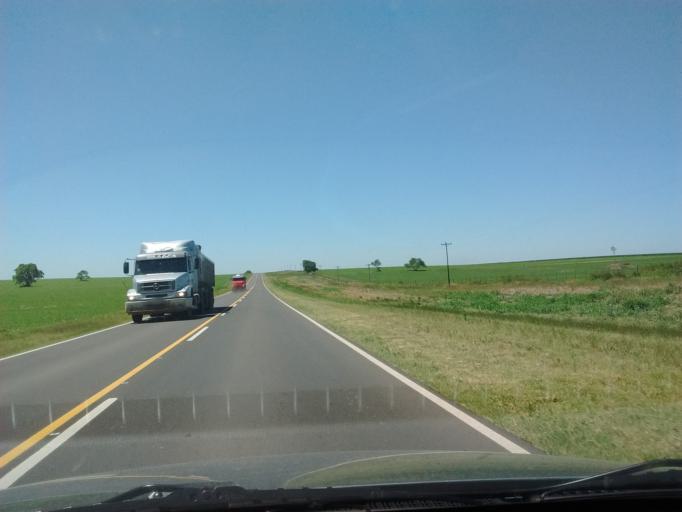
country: AR
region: Entre Rios
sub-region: Departamento de Victoria
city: Victoria
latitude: -32.7951
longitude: -59.8969
